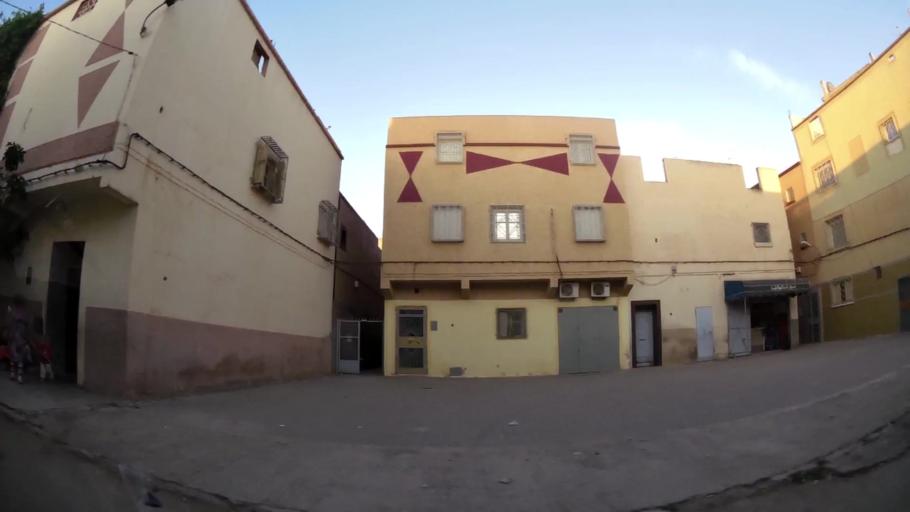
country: MA
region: Oriental
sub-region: Oujda-Angad
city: Oujda
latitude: 34.7013
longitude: -1.9202
